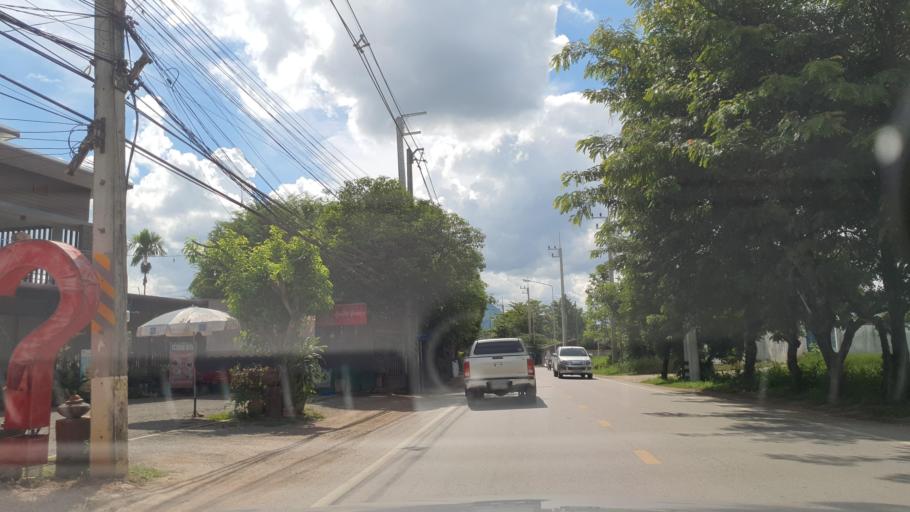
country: TH
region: Chiang Mai
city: Mae Wang
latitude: 18.6022
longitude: 98.8070
